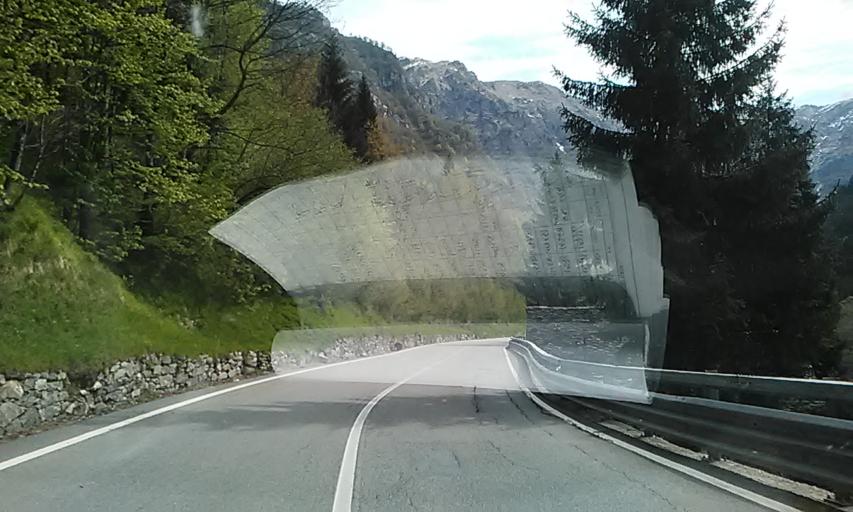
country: IT
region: Piedmont
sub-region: Provincia di Vercelli
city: Mollia
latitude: 45.8190
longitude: 7.9995
